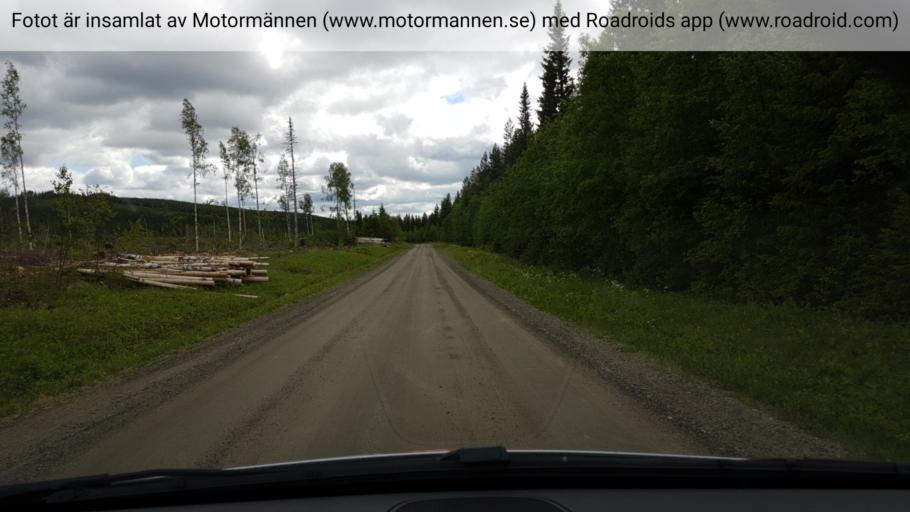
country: SE
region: Jaemtland
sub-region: Ragunda Kommun
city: Hammarstrand
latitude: 62.8785
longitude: 16.0596
